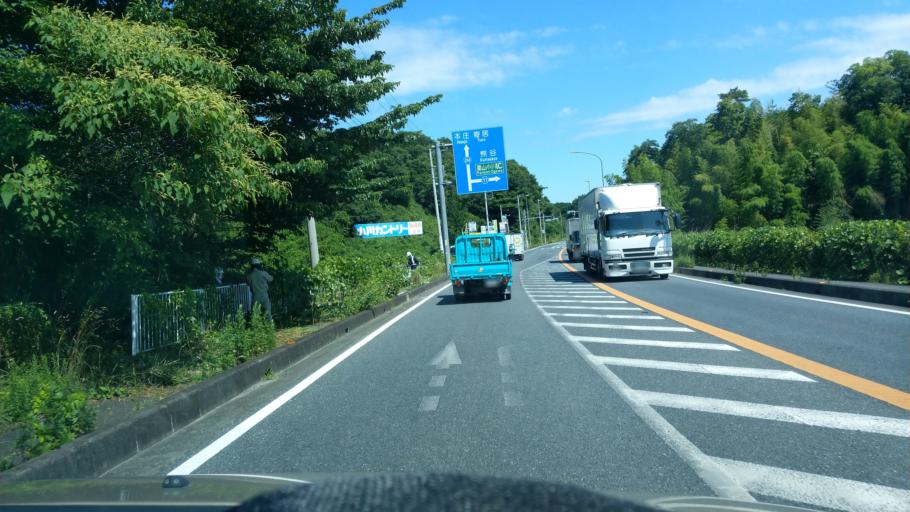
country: JP
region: Saitama
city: Ogawa
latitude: 36.0625
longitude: 139.2904
